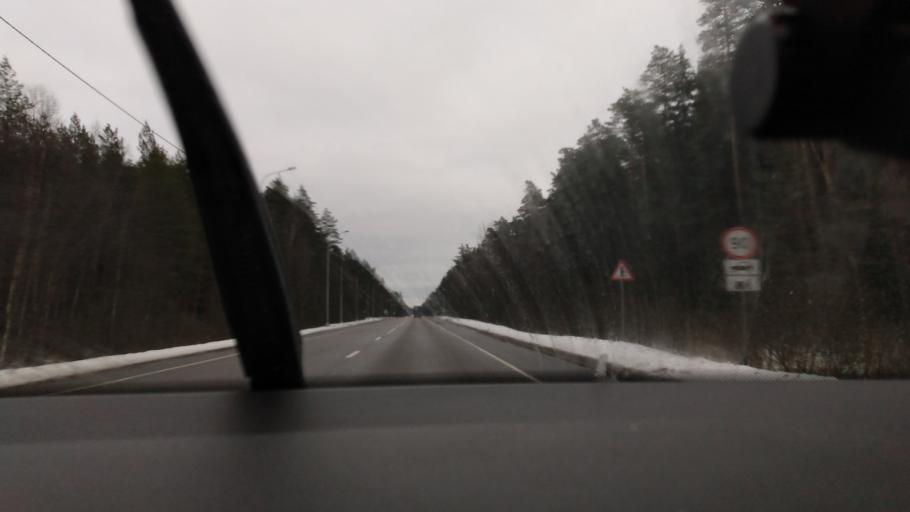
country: RU
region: Moskovskaya
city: Il'inskiy Pogost
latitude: 55.4608
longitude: 38.9828
